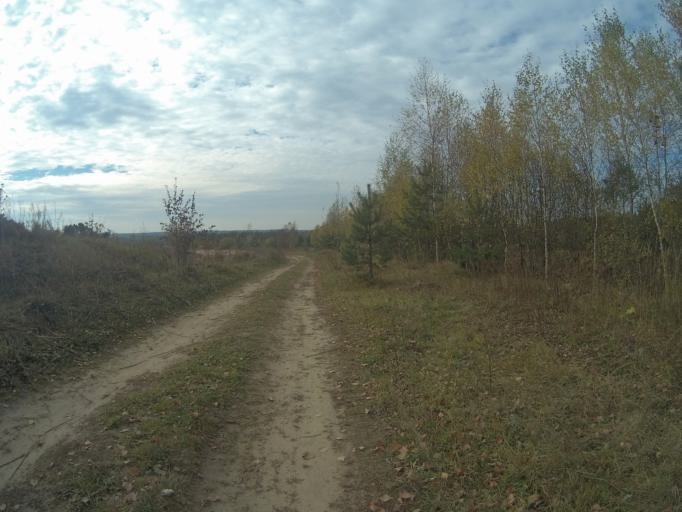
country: RU
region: Vladimir
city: Kommunar
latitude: 56.0867
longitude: 40.4946
